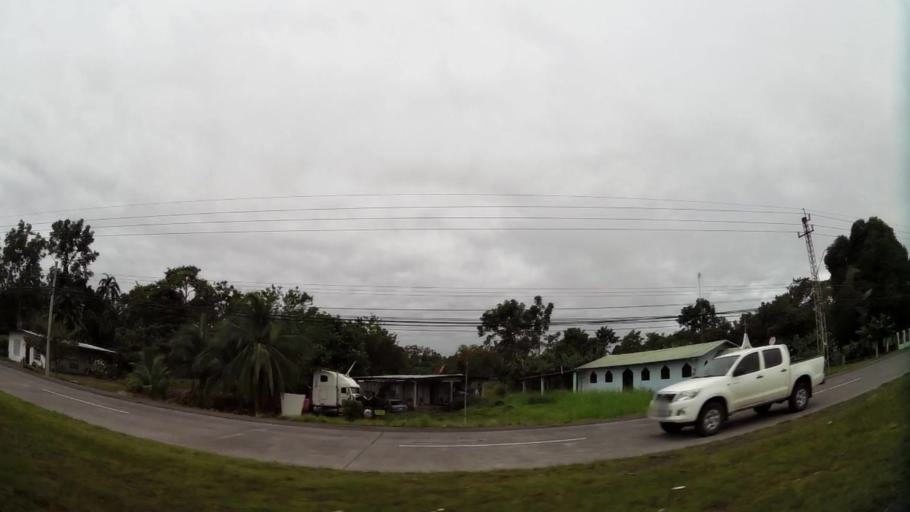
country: PA
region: Chiriqui
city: Boqueron
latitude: 8.4942
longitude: -82.5845
